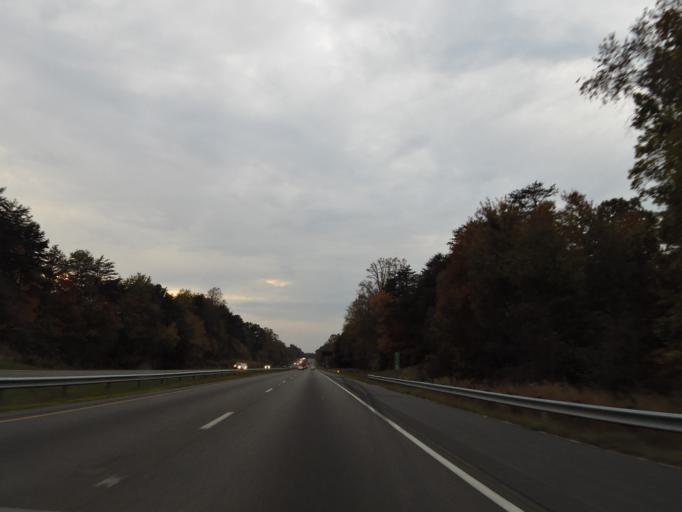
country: US
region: North Carolina
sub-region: Burke County
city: Icard
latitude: 35.7267
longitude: -81.4896
